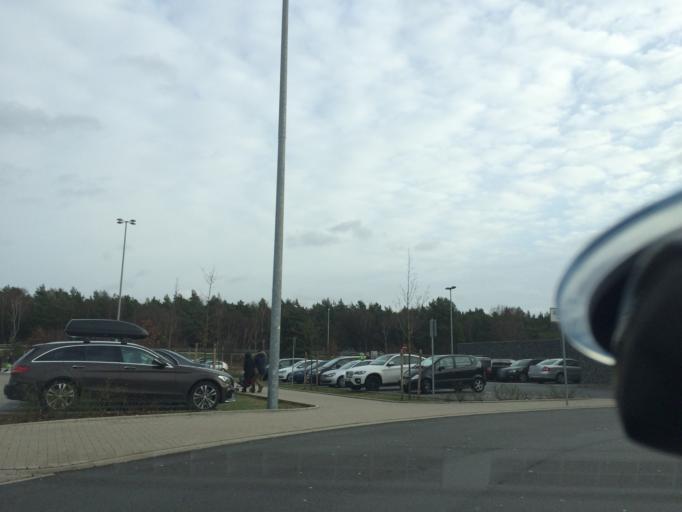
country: DE
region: Lower Saxony
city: Soltau
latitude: 52.9831
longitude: 9.9258
